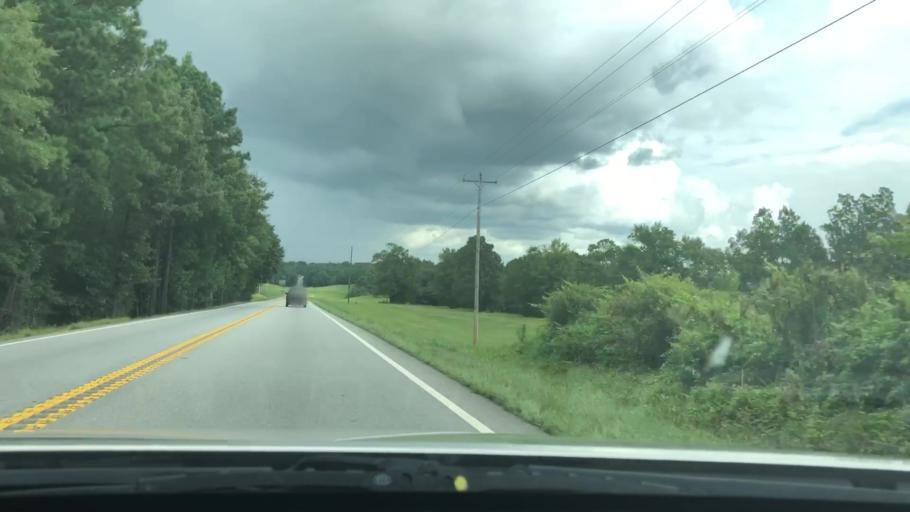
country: US
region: Georgia
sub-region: Lamar County
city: Barnesville
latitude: 33.1796
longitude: -84.0824
